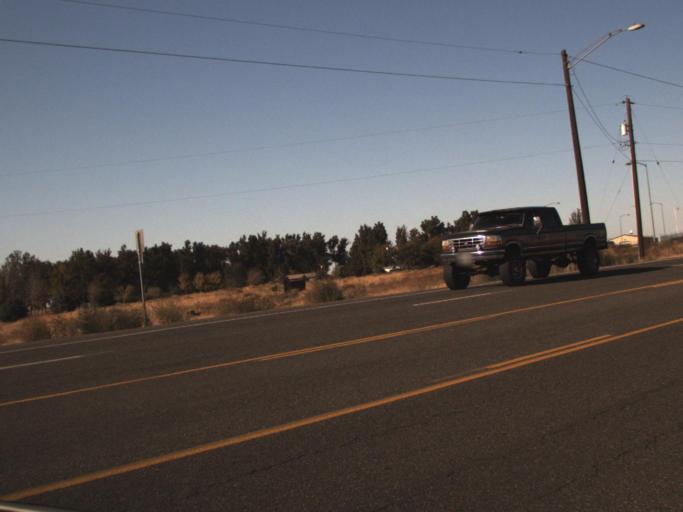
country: US
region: Washington
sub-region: Franklin County
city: Pasco
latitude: 46.2459
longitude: -119.0853
